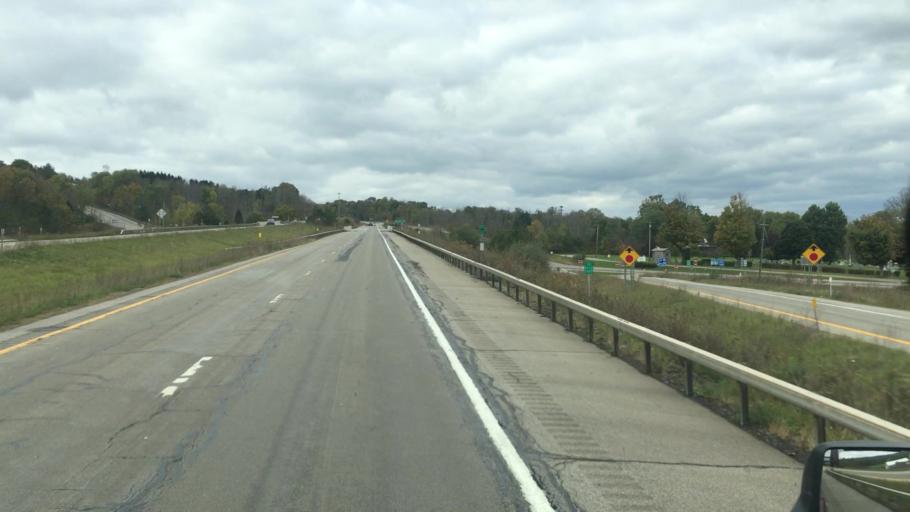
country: US
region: New York
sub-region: Cattaraugus County
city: Randolph
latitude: 42.1576
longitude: -78.9916
